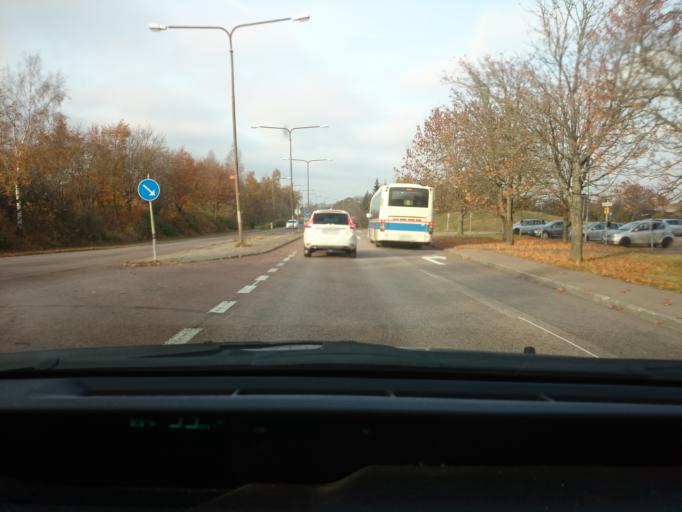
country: SE
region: Vaestmanland
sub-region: Vasteras
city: Vasteras
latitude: 59.6406
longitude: 16.5070
